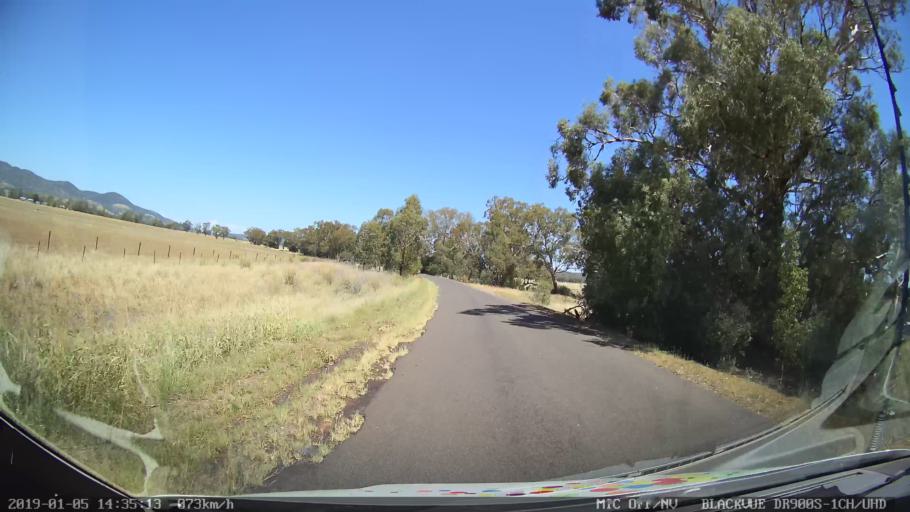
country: AU
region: New South Wales
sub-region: Tamworth Municipality
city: Phillip
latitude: -31.2397
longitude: 150.6479
